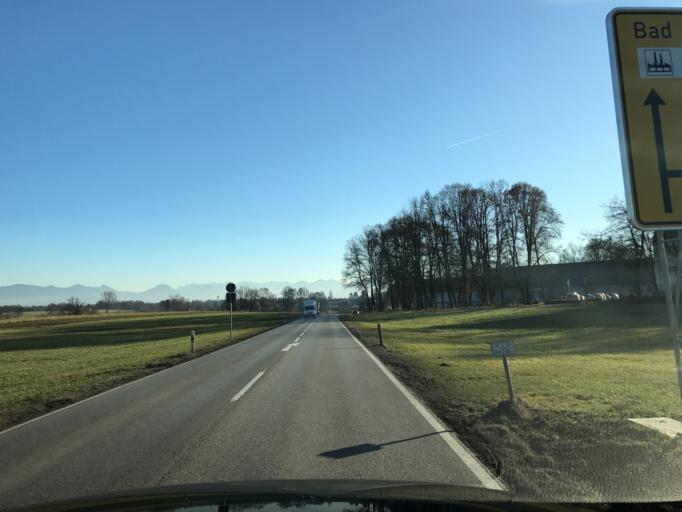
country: DE
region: Bavaria
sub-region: Upper Bavaria
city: Bad Aibling
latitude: 47.8872
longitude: 11.9909
